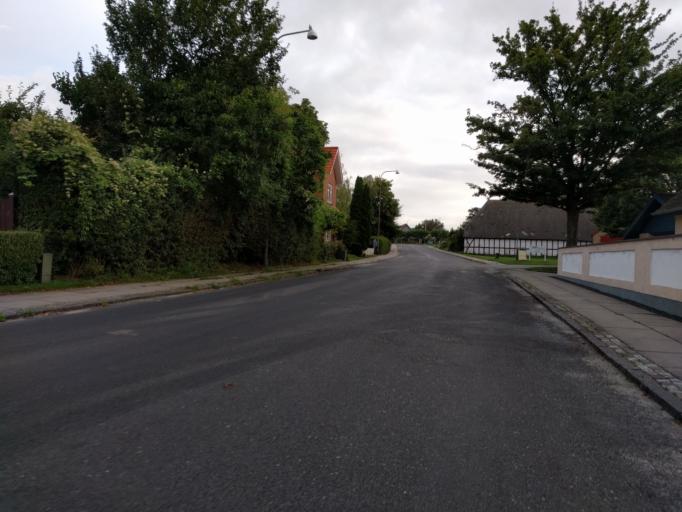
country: DK
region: South Denmark
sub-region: Kerteminde Kommune
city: Munkebo
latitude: 55.4580
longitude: 10.5604
